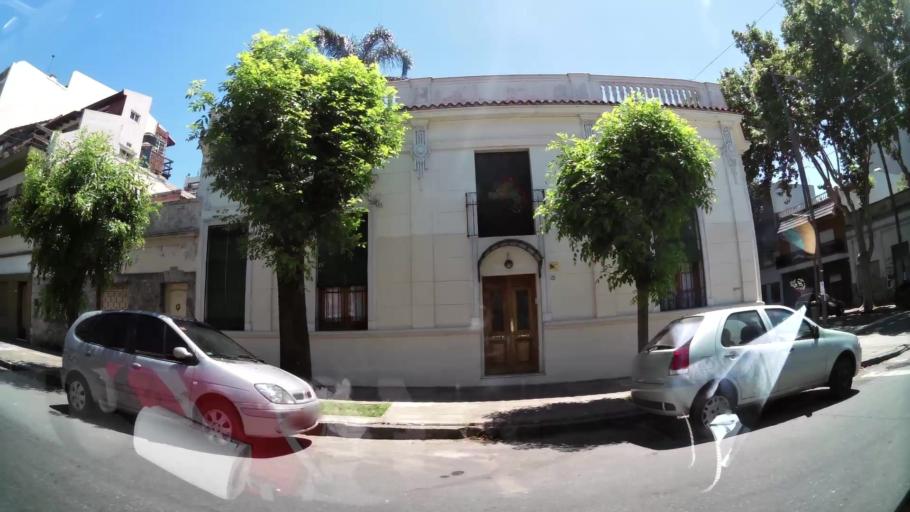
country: AR
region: Buenos Aires F.D.
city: Buenos Aires
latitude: -34.6373
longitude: -58.4002
